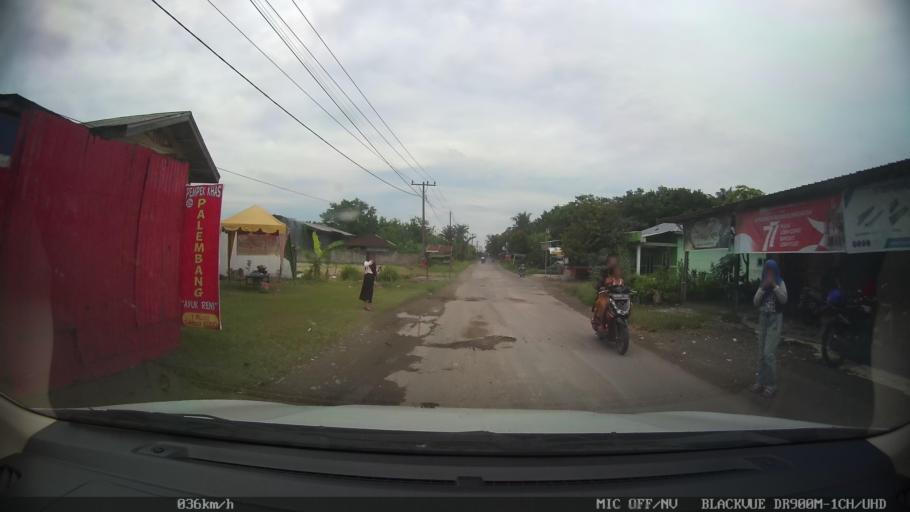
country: ID
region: North Sumatra
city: Binjai
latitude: 3.6424
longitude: 98.5512
